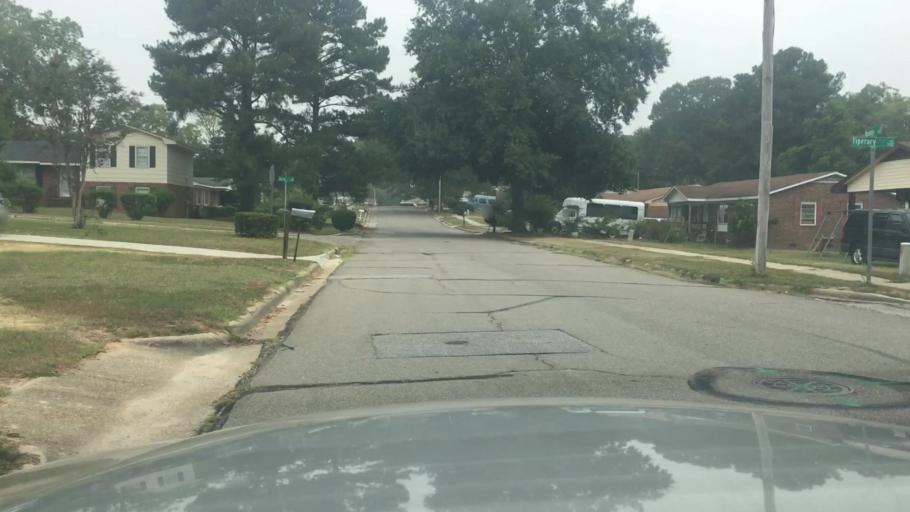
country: US
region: North Carolina
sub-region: Cumberland County
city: Fayetteville
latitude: 35.0686
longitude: -78.8860
